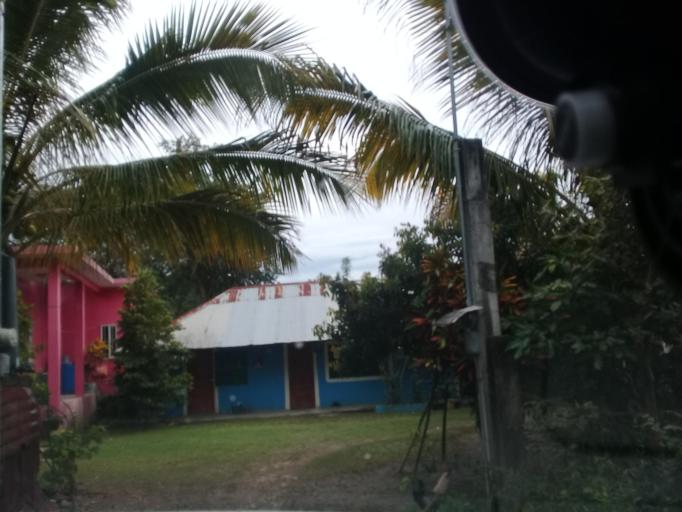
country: MX
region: Hidalgo
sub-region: Huejutla de Reyes
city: Chalahuiyapa
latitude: 21.1645
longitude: -98.3658
